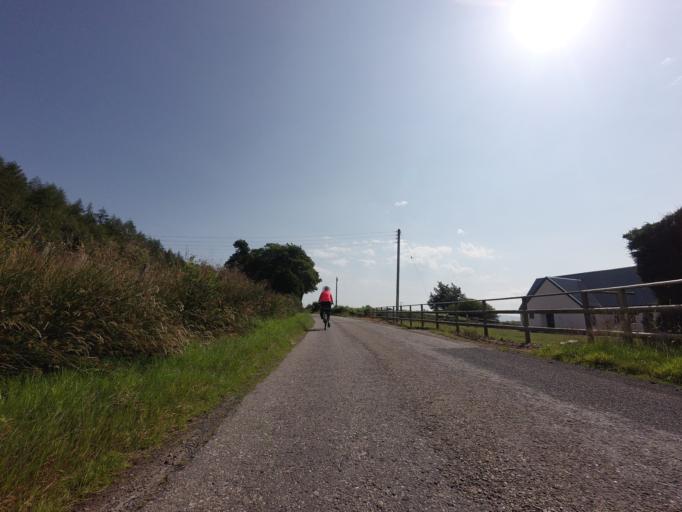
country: GB
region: Scotland
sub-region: Highland
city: Invergordon
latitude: 57.7586
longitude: -4.1262
